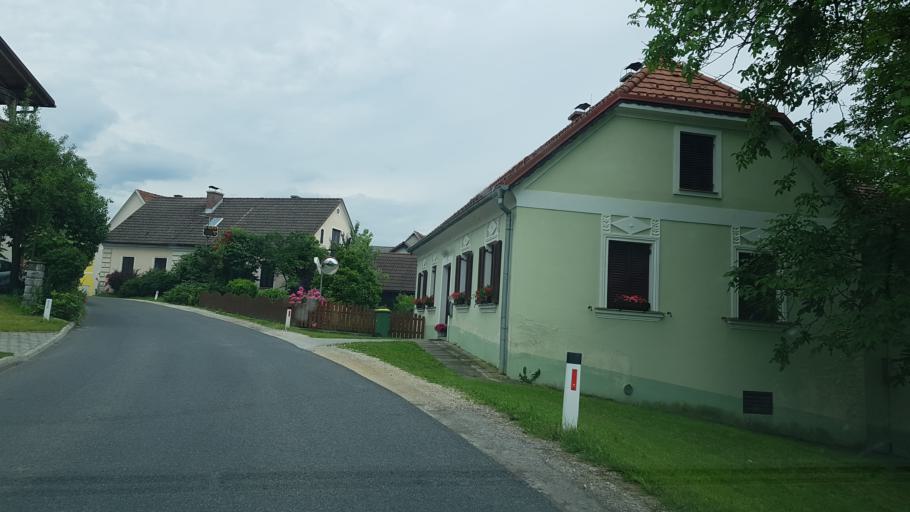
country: SI
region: Vojnik
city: Vojnik
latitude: 46.3131
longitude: 15.2842
